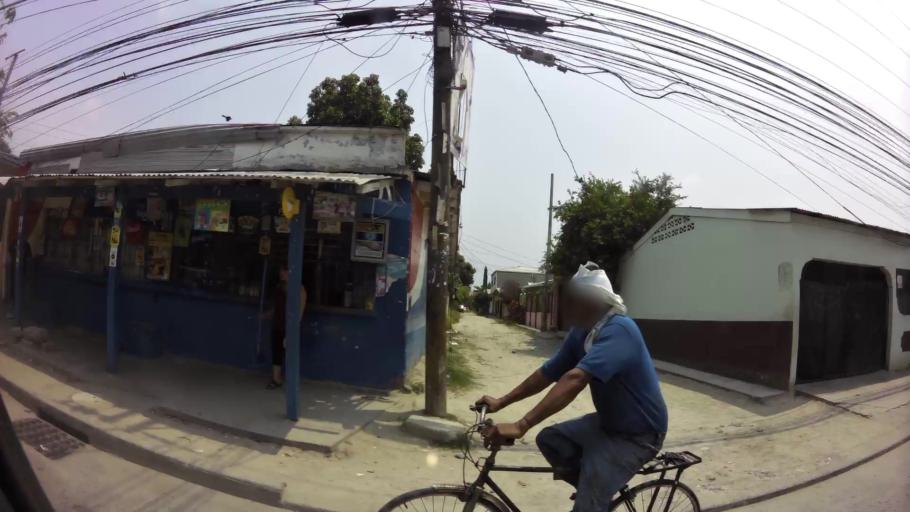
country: HN
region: Cortes
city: San Pedro Sula
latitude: 15.4912
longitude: -87.9950
